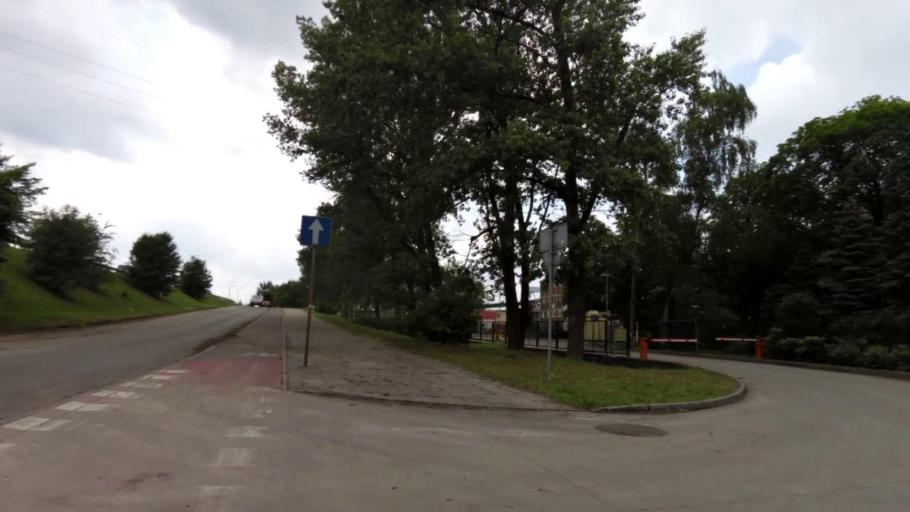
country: PL
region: West Pomeranian Voivodeship
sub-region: Szczecin
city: Szczecin
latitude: 53.4096
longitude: 14.5852
